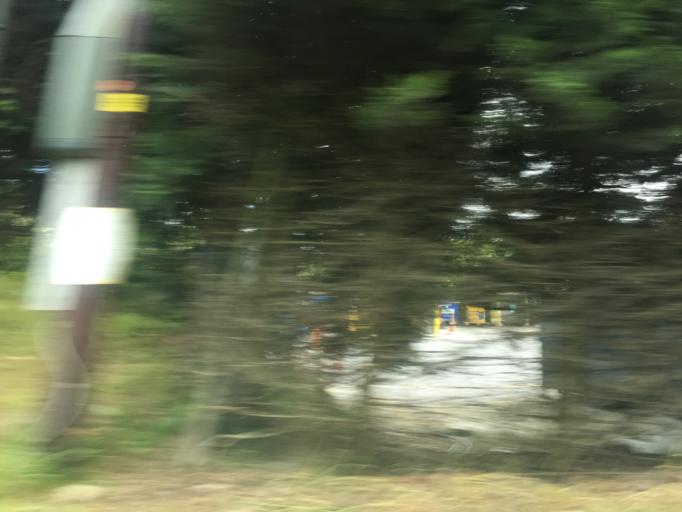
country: GB
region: Wales
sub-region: County of Ceredigion
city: Lampeter
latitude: 52.1217
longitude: -4.0781
